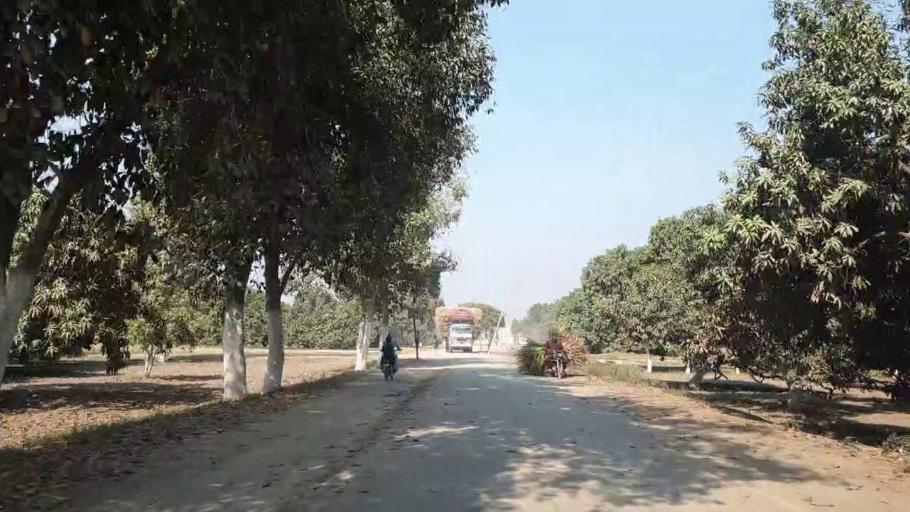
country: PK
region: Sindh
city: Tando Allahyar
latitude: 25.4897
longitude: 68.8226
